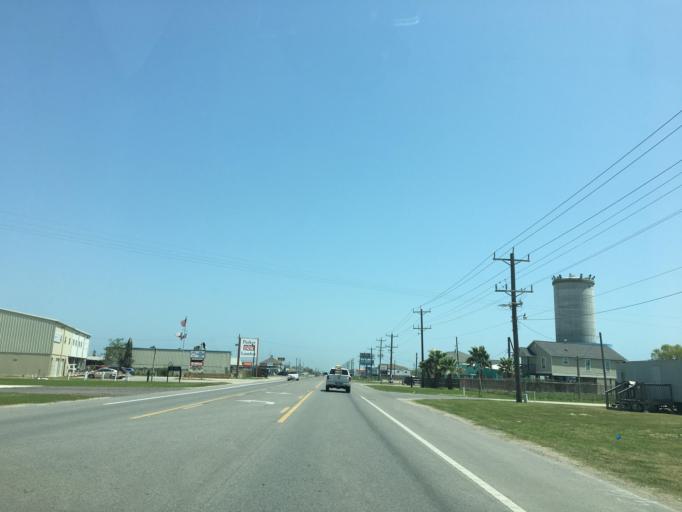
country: US
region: Texas
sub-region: Galveston County
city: Bolivar Peninsula
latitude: 29.4577
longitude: -94.6387
